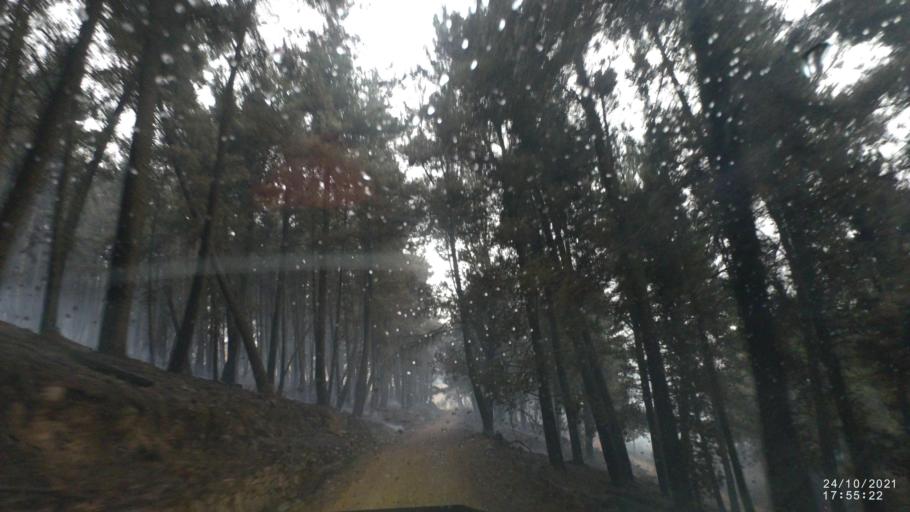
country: BO
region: Cochabamba
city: Cochabamba
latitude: -17.3219
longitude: -66.1287
